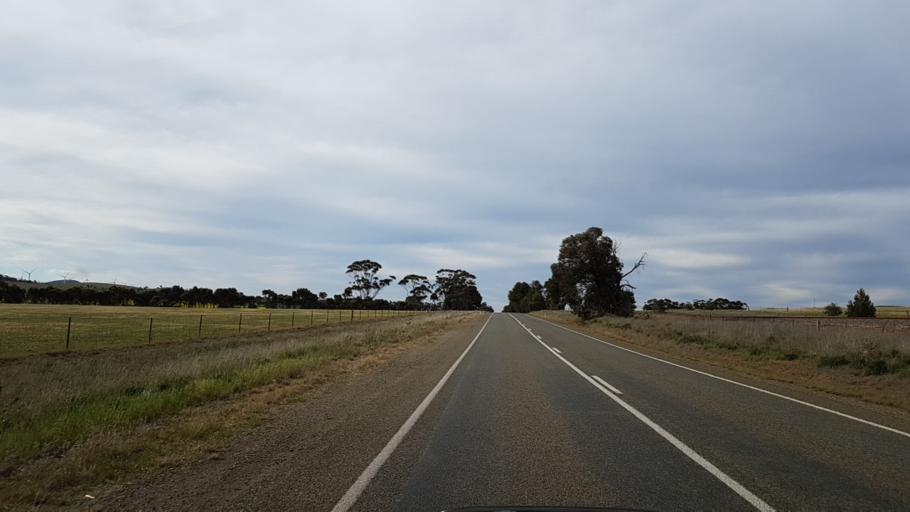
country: AU
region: South Australia
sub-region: Northern Areas
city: Jamestown
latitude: -33.1575
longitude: 138.6142
